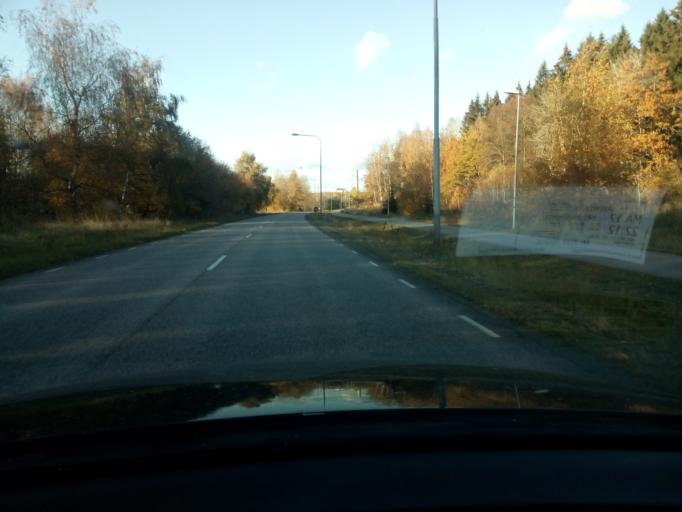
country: SE
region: Soedermanland
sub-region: Nykopings Kommun
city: Nykoping
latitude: 58.7327
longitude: 17.0075
